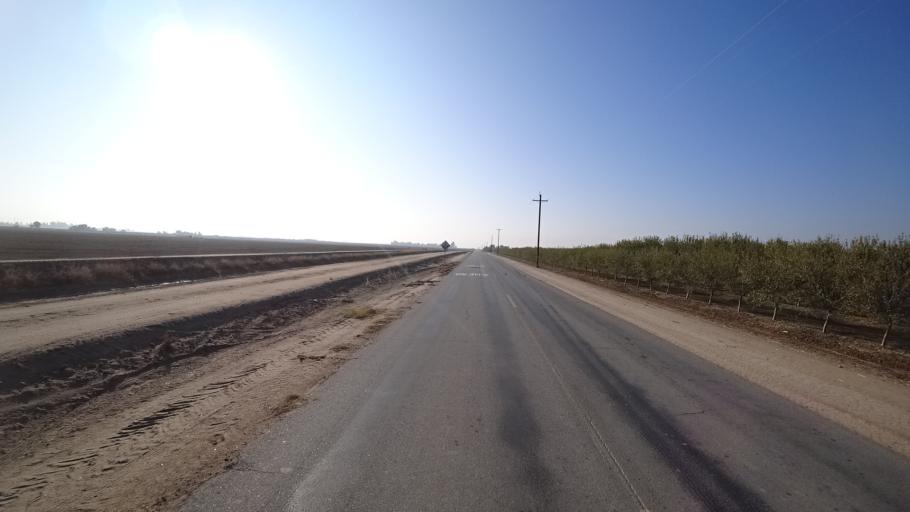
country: US
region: California
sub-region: Kern County
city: Greenfield
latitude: 35.2504
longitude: -118.9854
